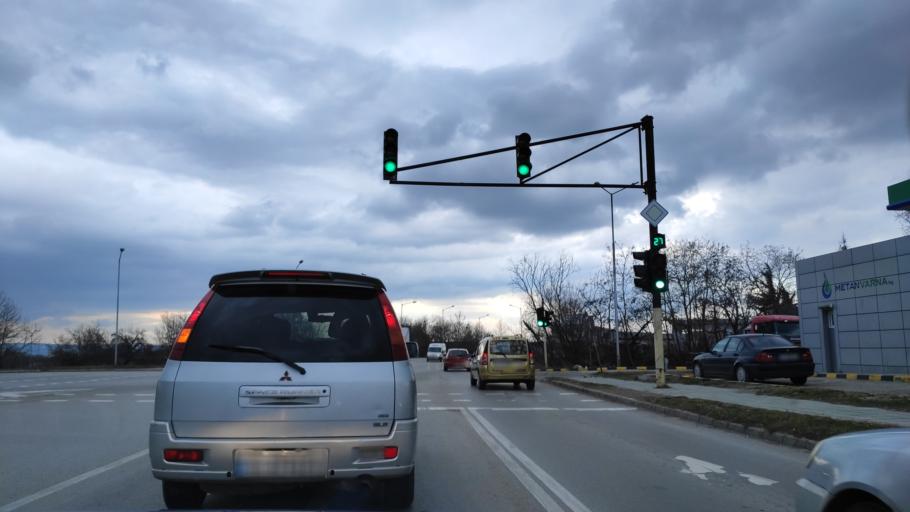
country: BG
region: Varna
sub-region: Obshtina Aksakovo
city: Aksakovo
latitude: 43.2334
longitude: 27.8645
